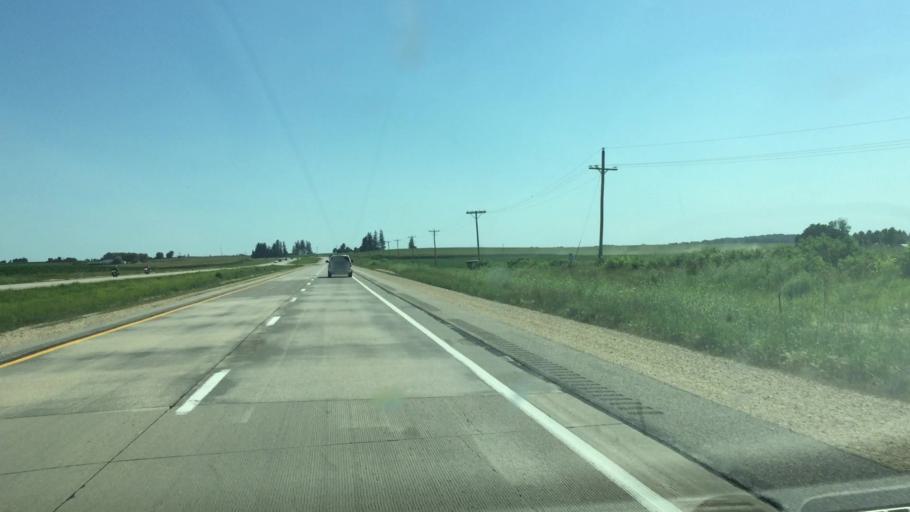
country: US
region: Iowa
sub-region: Jones County
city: Monticello
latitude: 42.1830
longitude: -91.2226
